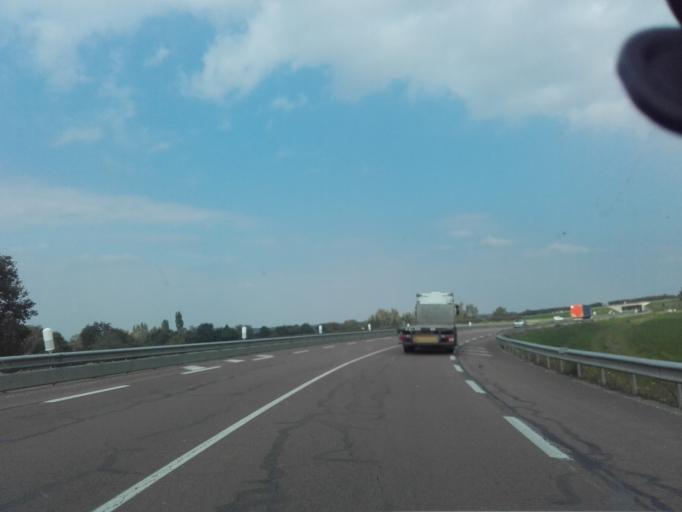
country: FR
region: Bourgogne
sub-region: Departement de Saone-et-Loire
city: Champforgeuil
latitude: 46.8119
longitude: 4.8244
